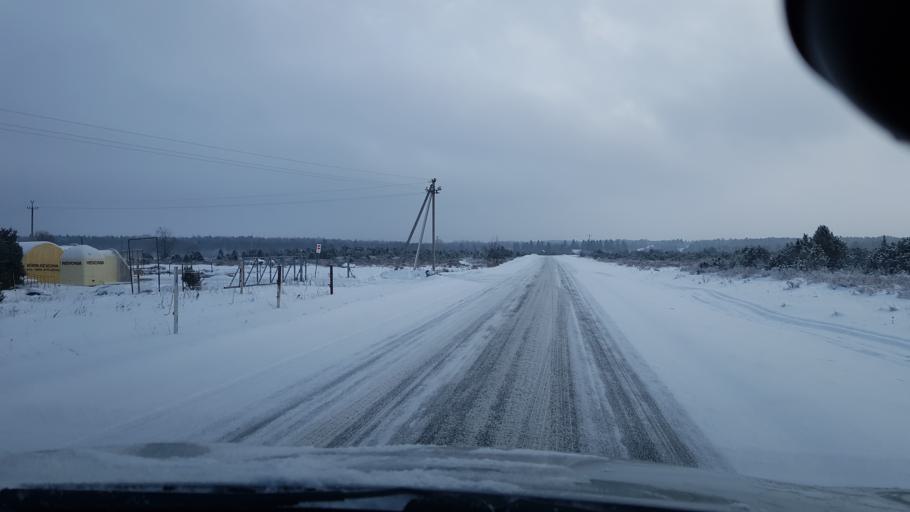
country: EE
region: Harju
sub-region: Keila linn
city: Keila
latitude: 59.3868
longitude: 24.3986
